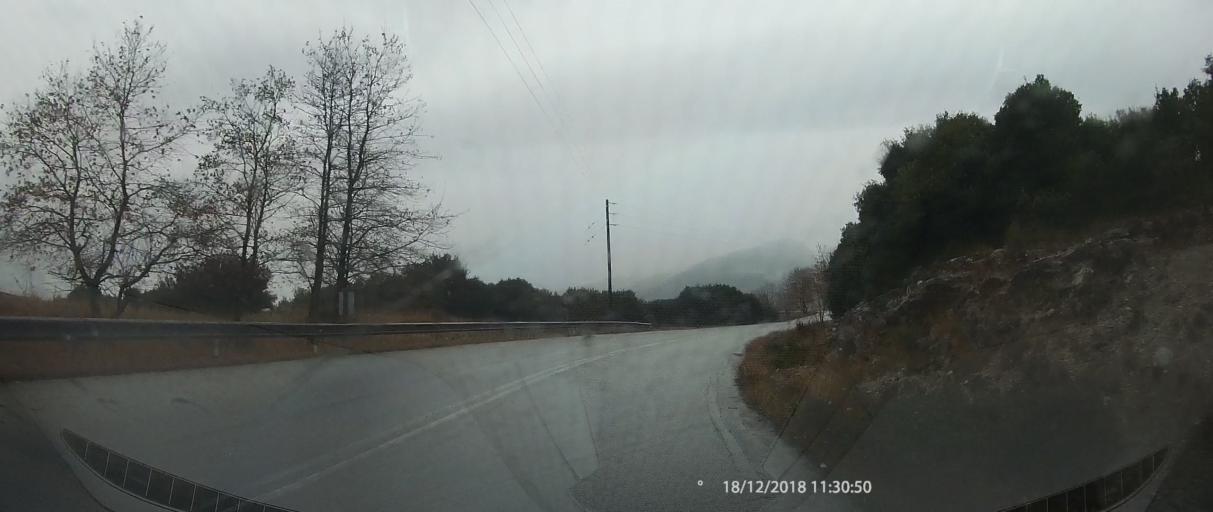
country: GR
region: Central Macedonia
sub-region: Nomos Pierias
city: Litochoro
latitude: 40.1185
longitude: 22.5183
